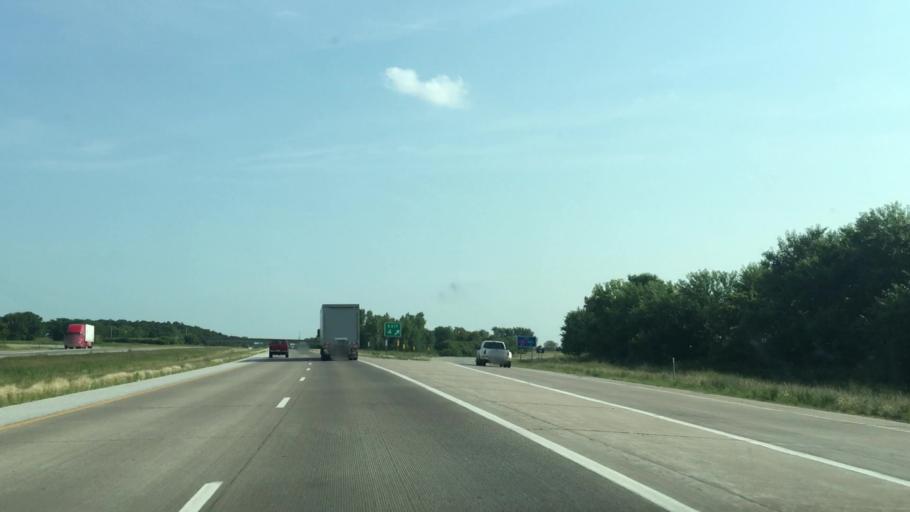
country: US
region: Iowa
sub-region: Scott County
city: Blue Grass
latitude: 41.5431
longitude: -90.6782
